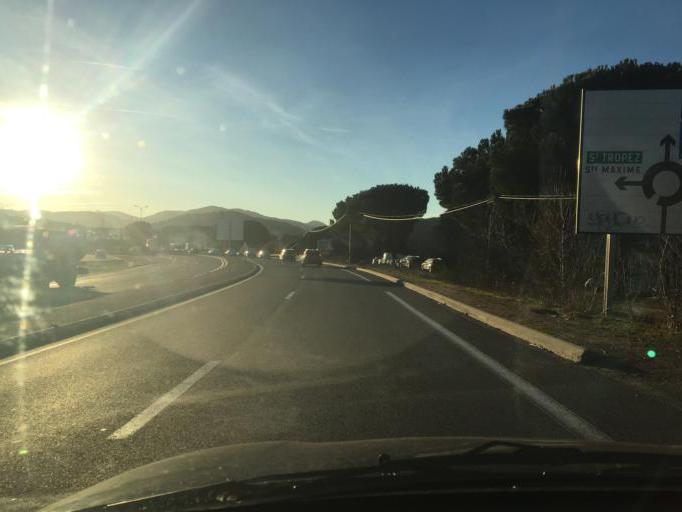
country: FR
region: Provence-Alpes-Cote d'Azur
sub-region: Departement du Var
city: Le Muy
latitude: 43.4643
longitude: 6.5464
